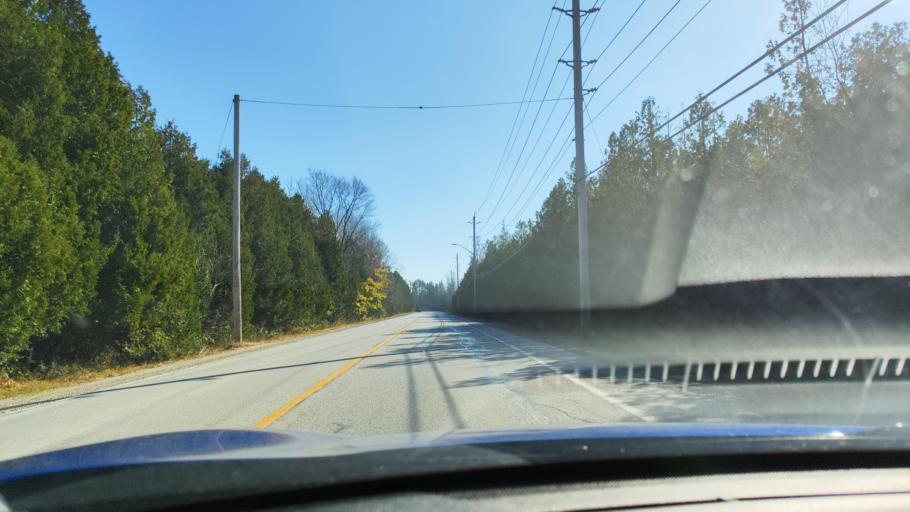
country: CA
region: Ontario
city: Wasaga Beach
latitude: 44.5035
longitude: -79.9907
